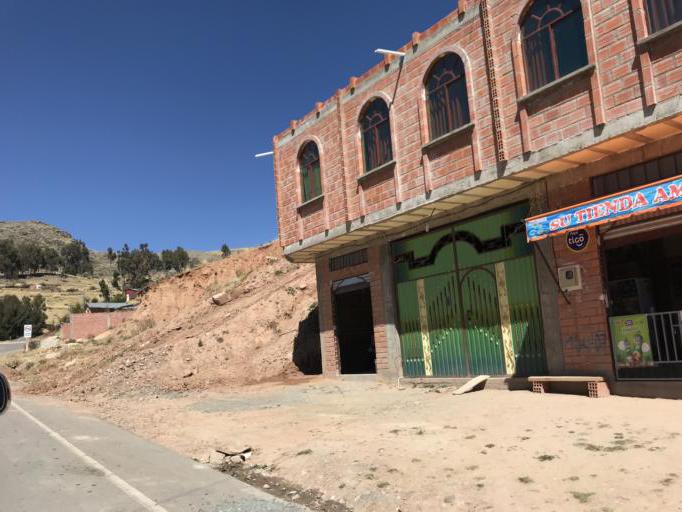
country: PE
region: Puno
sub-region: Yunguyo
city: Yunguyo
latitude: -16.1718
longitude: -69.0773
